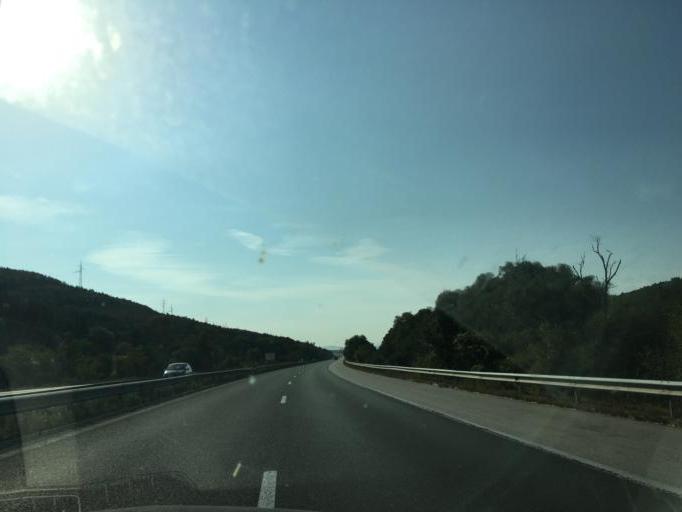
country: BG
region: Sofiya
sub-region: Obshtina Ikhtiman
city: Ikhtiman
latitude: 42.5073
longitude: 23.7648
